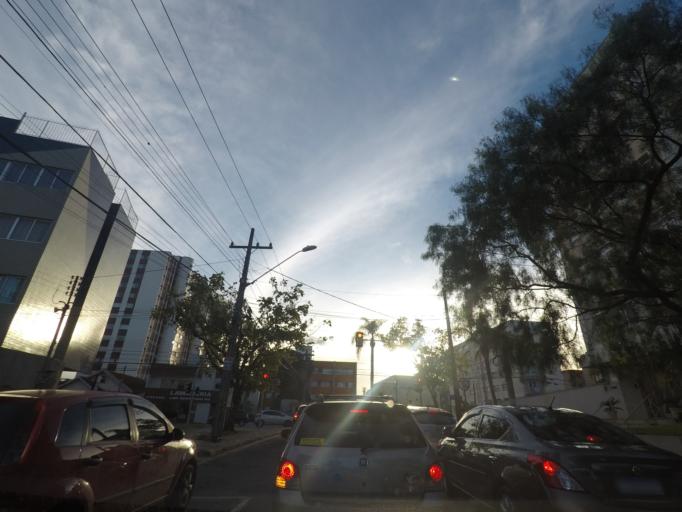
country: BR
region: Parana
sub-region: Curitiba
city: Curitiba
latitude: -25.4122
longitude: -49.2633
